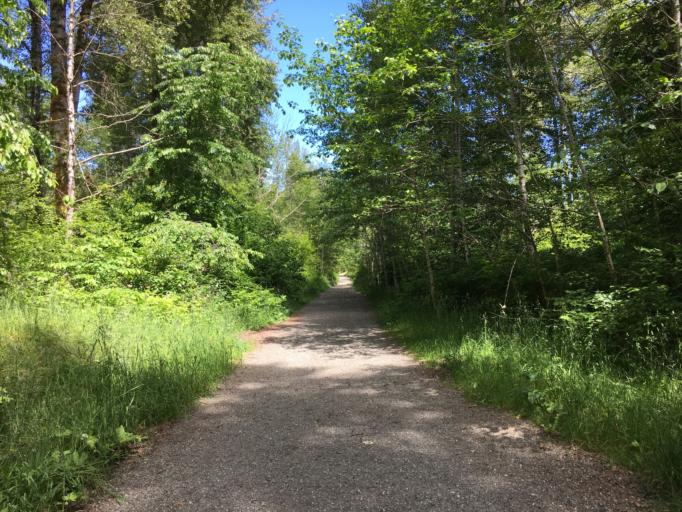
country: CA
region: British Columbia
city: Cumberland
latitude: 49.6152
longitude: -125.0505
